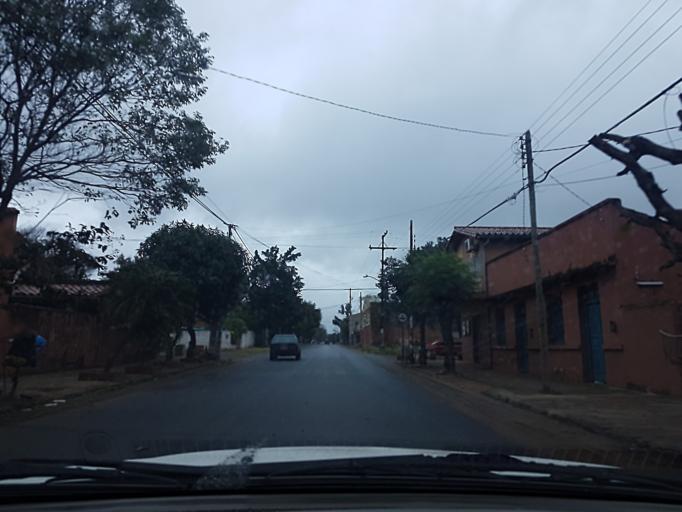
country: PY
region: Central
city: San Lorenzo
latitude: -25.2694
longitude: -57.4791
